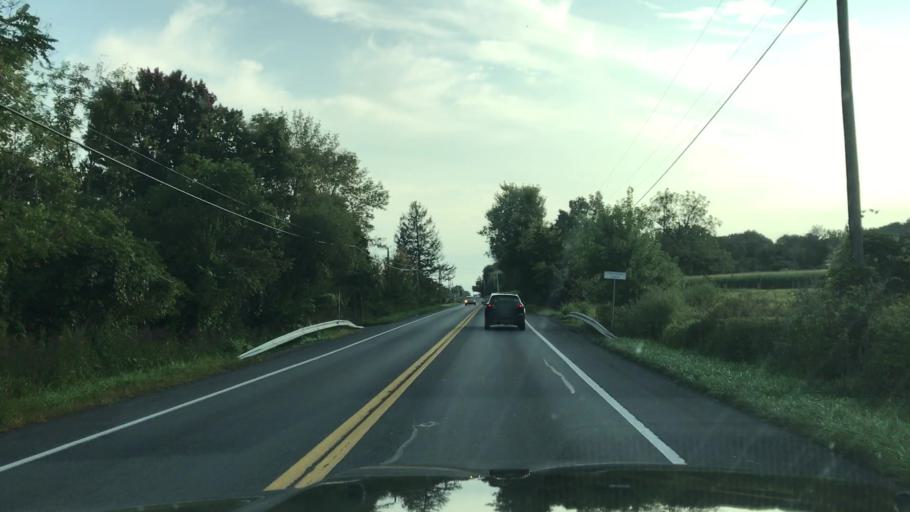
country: US
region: Pennsylvania
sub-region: Berks County
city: Bally
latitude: 40.4162
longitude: -75.5751
